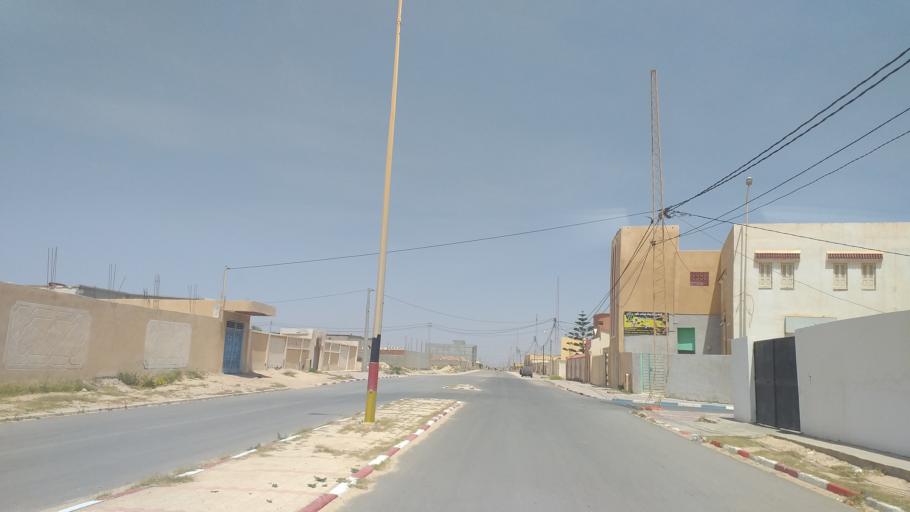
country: TN
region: Qabis
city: Gabes
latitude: 33.9516
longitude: 10.0685
